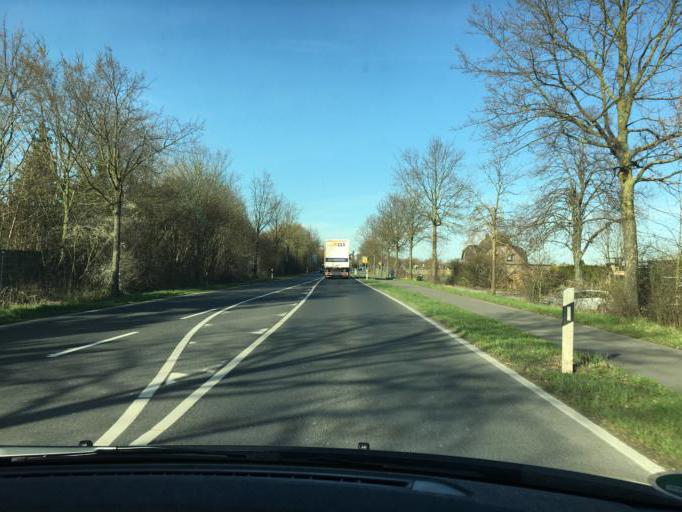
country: DE
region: North Rhine-Westphalia
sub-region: Regierungsbezirk Dusseldorf
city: Kaarst
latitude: 51.1921
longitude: 6.6143
